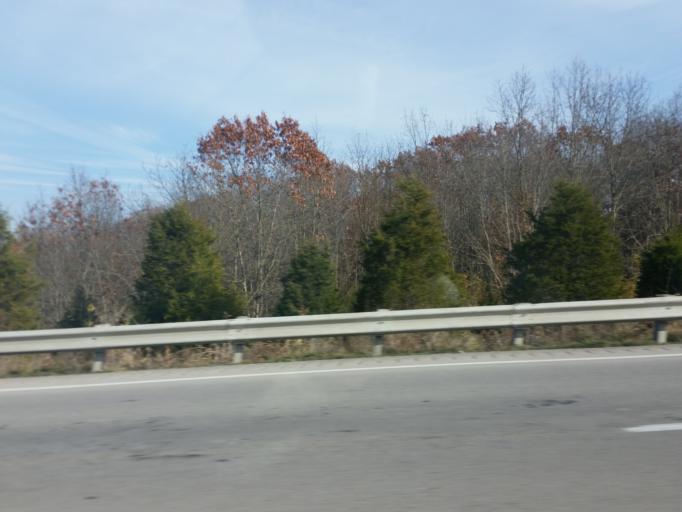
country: US
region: Kentucky
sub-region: Campbell County
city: Claryville
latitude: 38.8284
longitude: -84.3655
